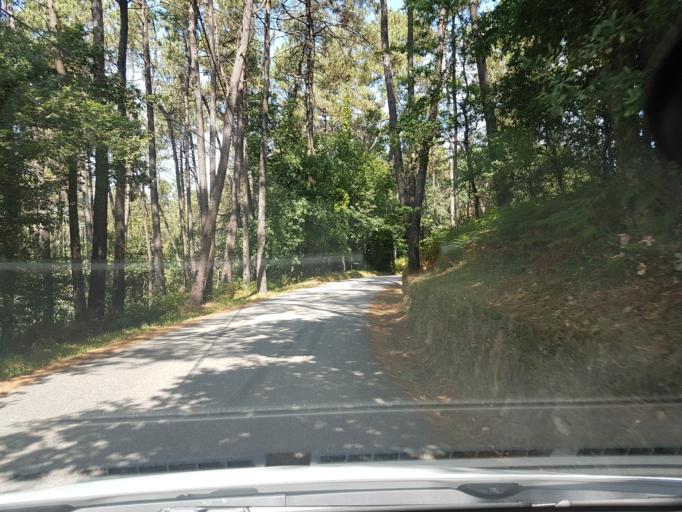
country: ES
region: Galicia
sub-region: Provincia de Pontevedra
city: Porrino
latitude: 42.1947
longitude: -8.6225
